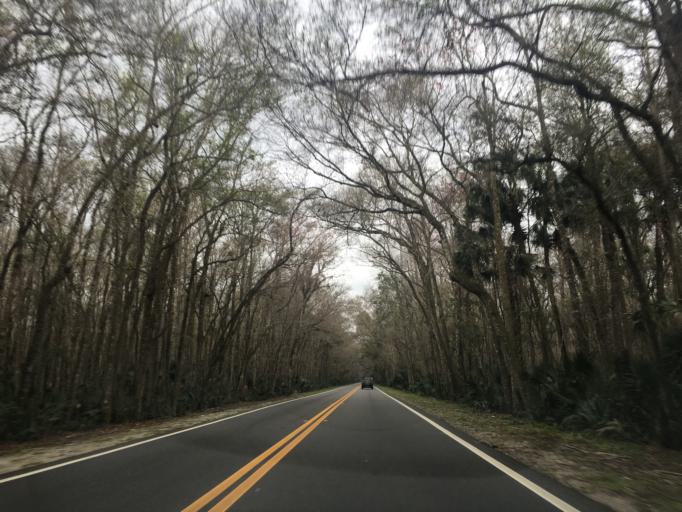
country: US
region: Florida
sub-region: Saint Johns County
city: Villano Beach
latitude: 30.0004
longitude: -81.4182
